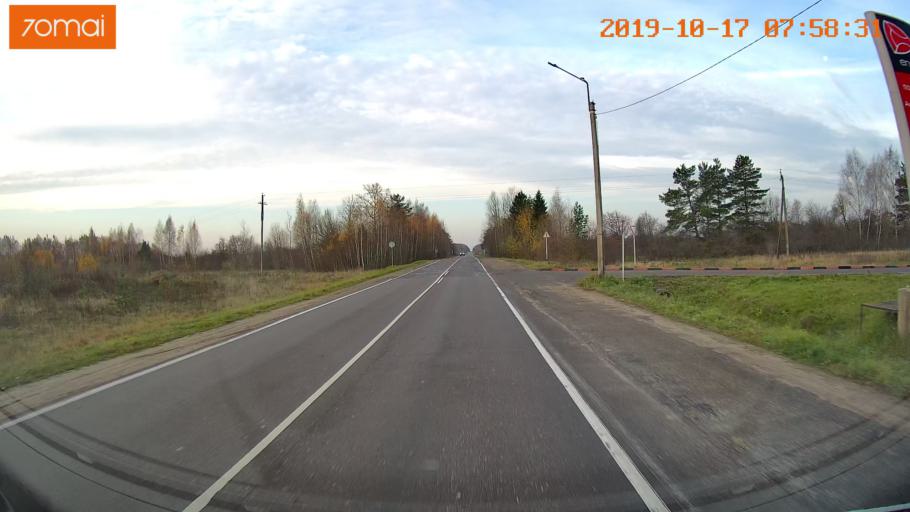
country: RU
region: Vladimir
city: Bavleny
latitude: 56.4019
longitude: 39.5559
